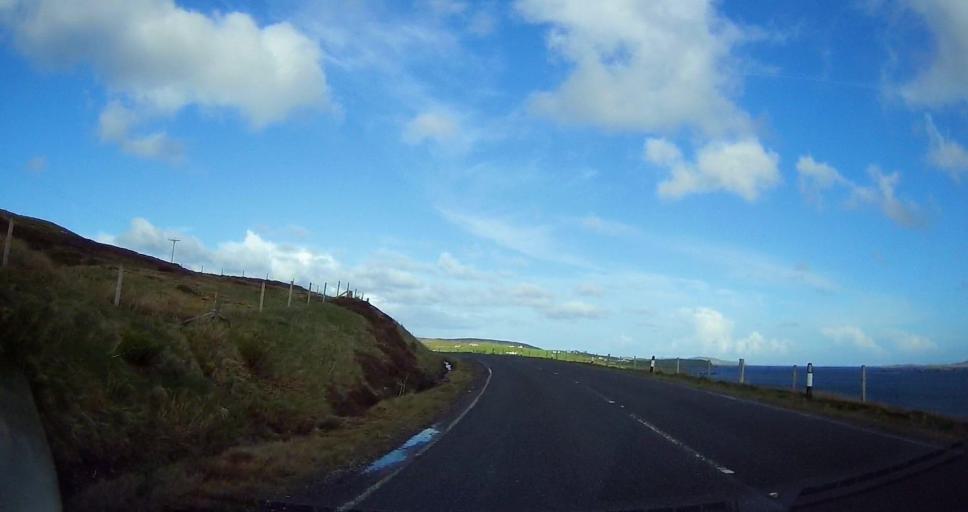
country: GB
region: Scotland
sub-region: Shetland Islands
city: Lerwick
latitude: 60.3526
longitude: -1.1799
